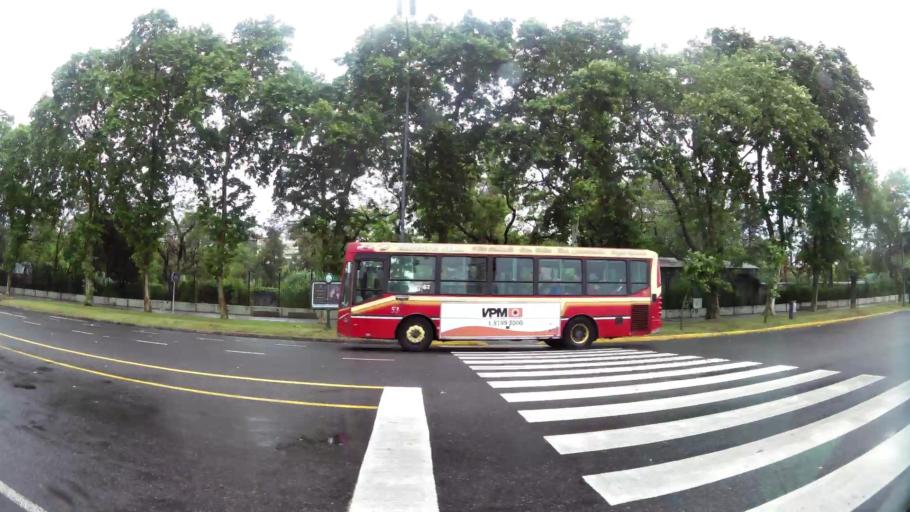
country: AR
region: Buenos Aires F.D.
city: Colegiales
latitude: -34.5771
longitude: -58.4171
